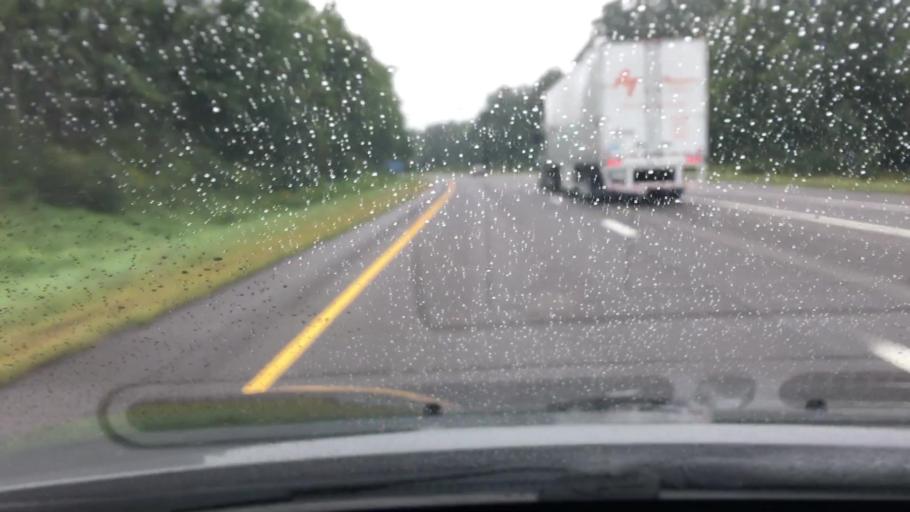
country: US
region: Pennsylvania
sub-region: Wayne County
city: Hawley
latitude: 41.3614
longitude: -75.2064
